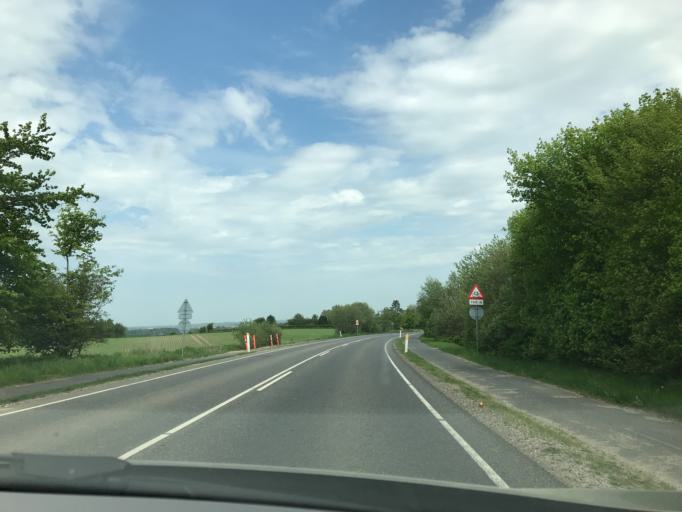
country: DK
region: South Denmark
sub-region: Assens Kommune
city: Assens
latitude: 55.2834
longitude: 9.9211
